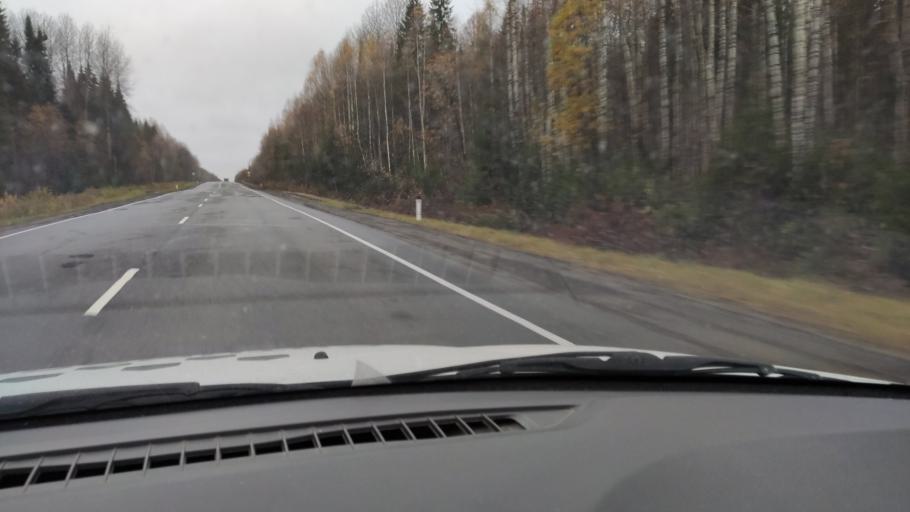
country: RU
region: Kirov
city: Omutninsk
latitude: 58.7609
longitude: 52.0092
